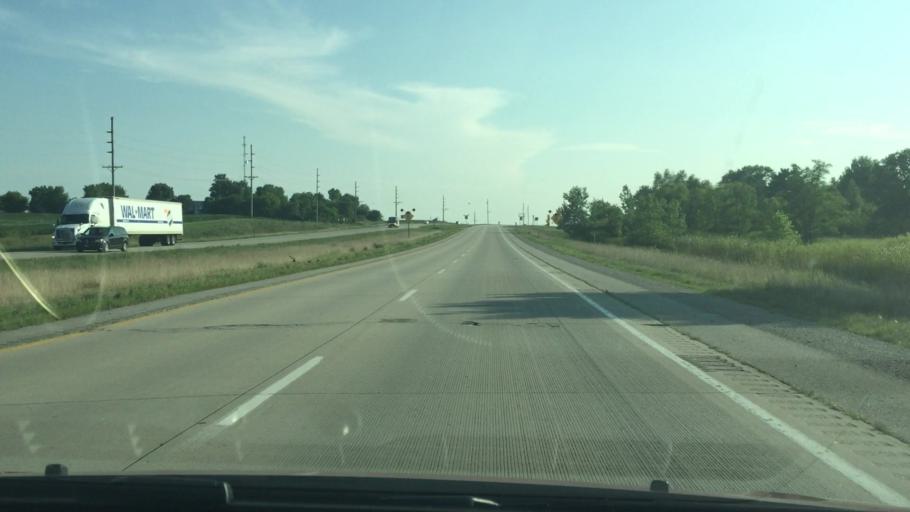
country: US
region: Iowa
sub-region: Muscatine County
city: Muscatine
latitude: 41.4695
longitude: -91.0031
